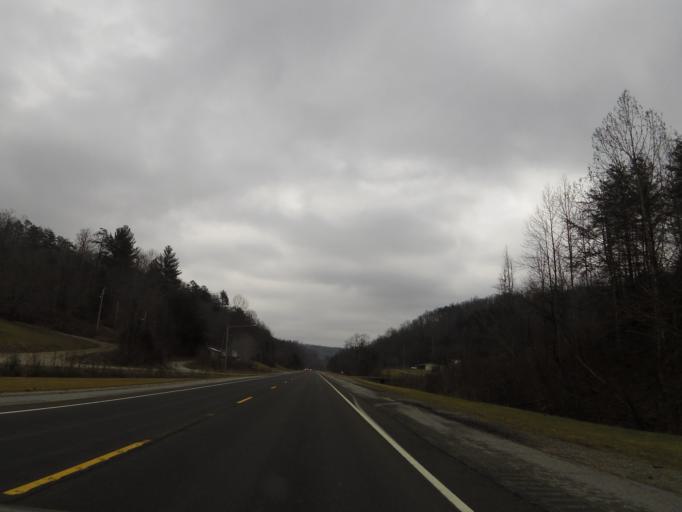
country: US
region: Tennessee
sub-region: Scott County
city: Huntsville
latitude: 36.4125
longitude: -84.4630
